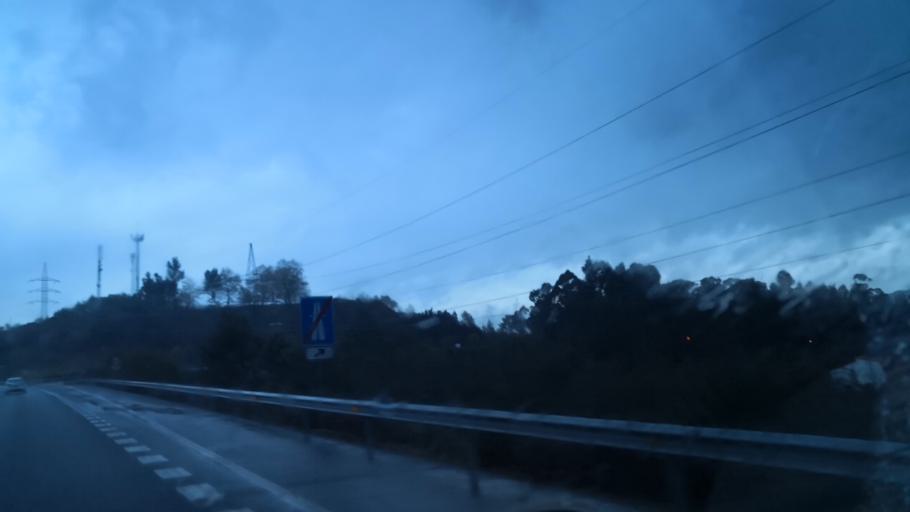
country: ES
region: Galicia
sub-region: Provincia de Pontevedra
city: Pontevedra
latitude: 42.3891
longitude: -8.6405
